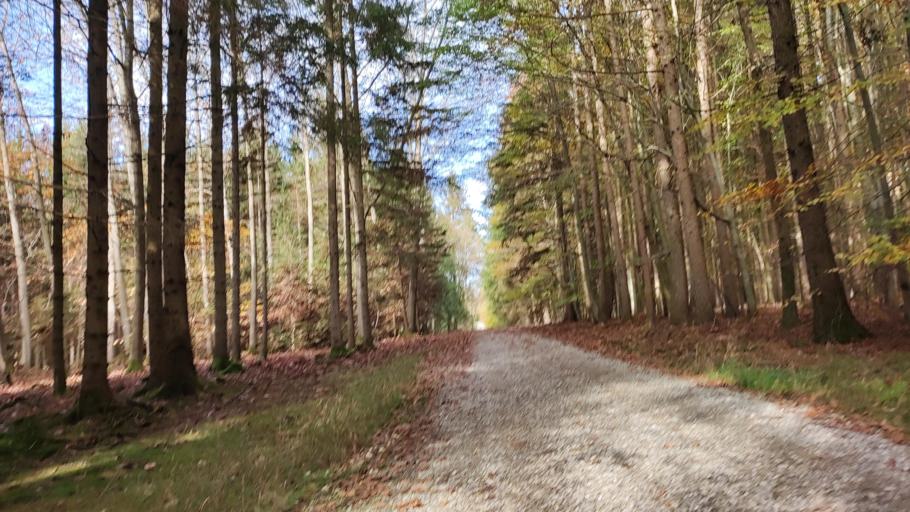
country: DE
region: Bavaria
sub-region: Swabia
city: Burtenbach
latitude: 48.3336
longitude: 10.4961
